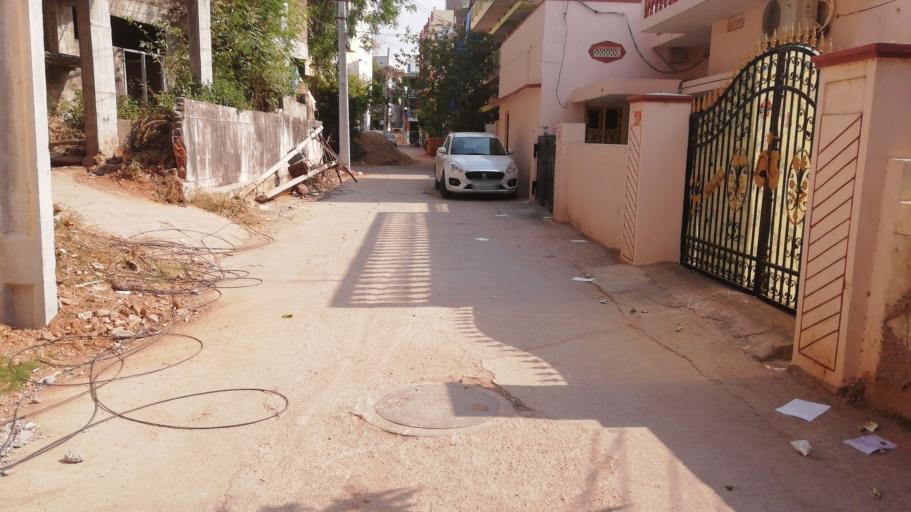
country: IN
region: Telangana
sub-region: Rangareddi
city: Gaddi Annaram
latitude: 17.3612
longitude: 78.5330
